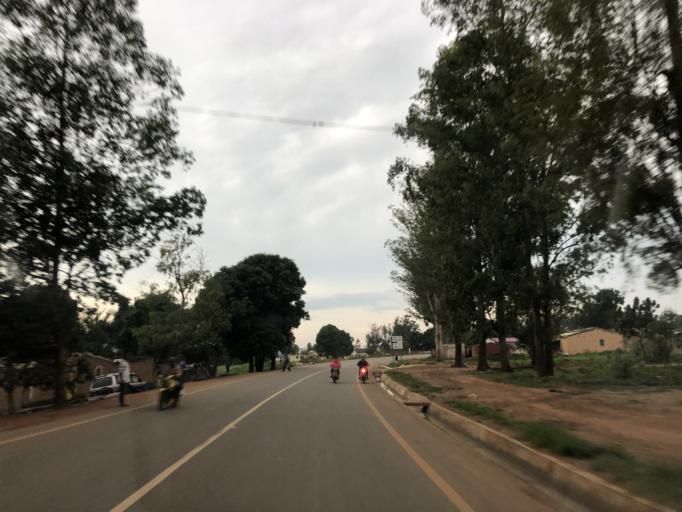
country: AO
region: Cuanza Sul
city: Uacu Cungo
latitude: -11.3522
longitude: 15.1186
